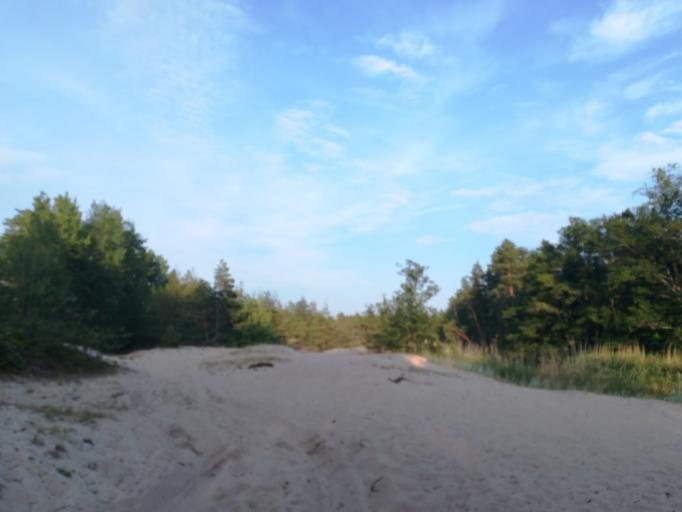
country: RU
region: Leningrad
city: Ust'-Luga
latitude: 59.6771
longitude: 28.2425
